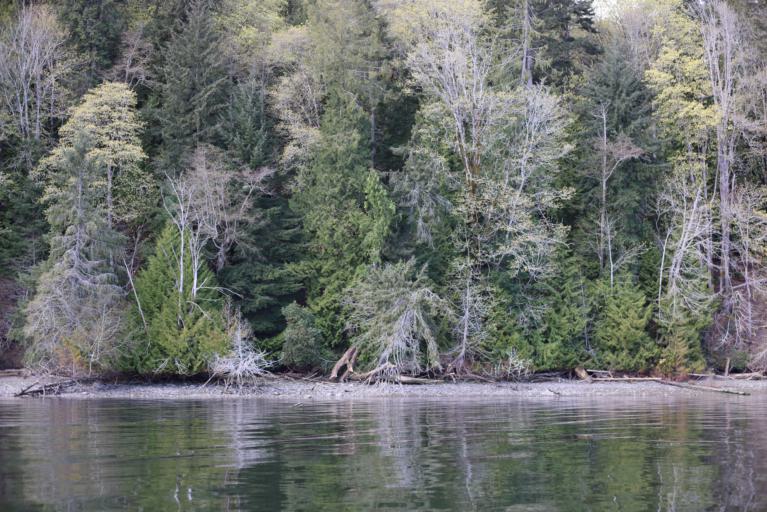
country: CA
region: British Columbia
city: North Saanich
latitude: 48.5997
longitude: -123.5217
